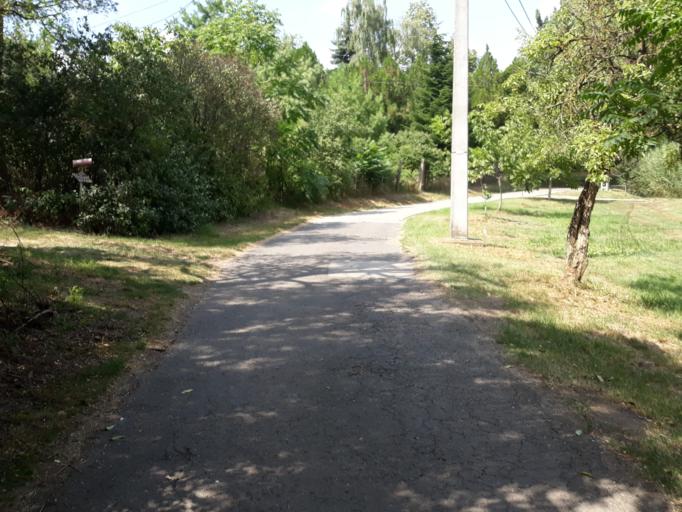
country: HU
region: Bekes
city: Oroshaza
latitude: 46.5632
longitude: 20.6246
